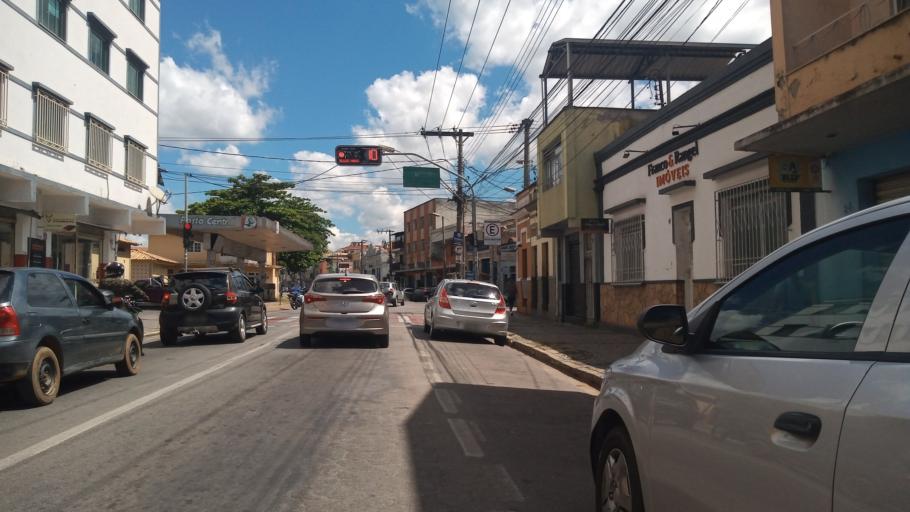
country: BR
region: Minas Gerais
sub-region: Sao Joao Del Rei
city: Sao Joao del Rei
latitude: -21.1309
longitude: -44.2539
